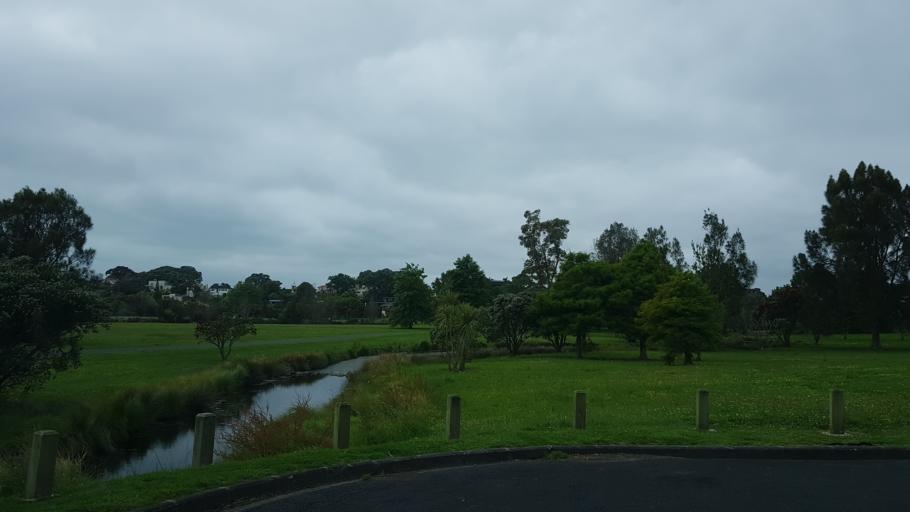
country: NZ
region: Auckland
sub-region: Auckland
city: North Shore
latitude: -36.8083
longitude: 174.7486
